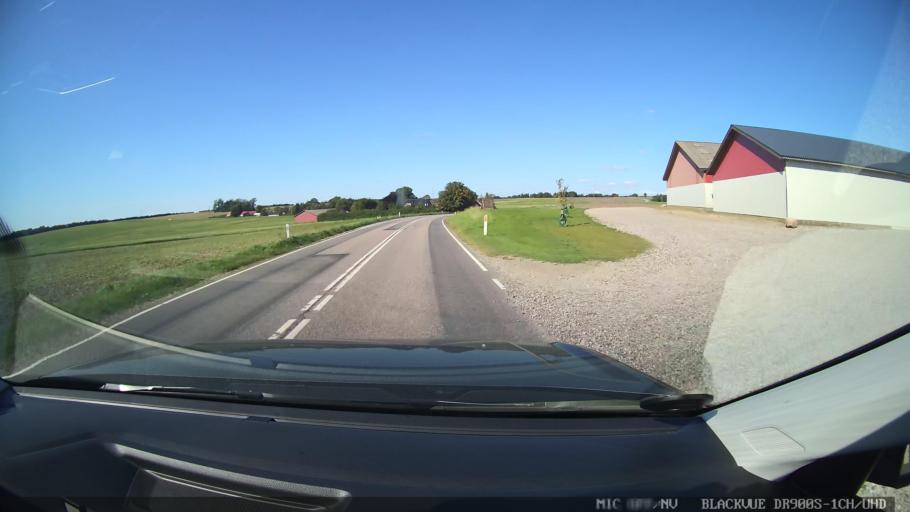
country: DK
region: Central Jutland
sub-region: Randers Kommune
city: Spentrup
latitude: 56.5872
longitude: 9.9965
